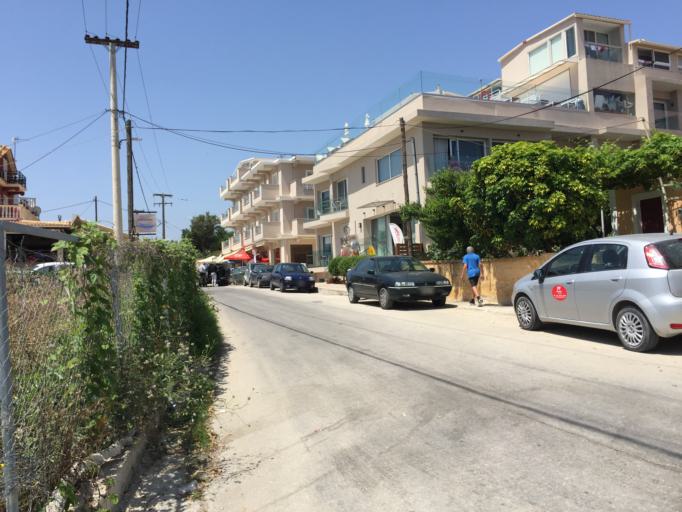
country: GR
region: Ionian Islands
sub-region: Nomos Zakynthou
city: Gaitanion
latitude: 37.8181
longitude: 20.8667
